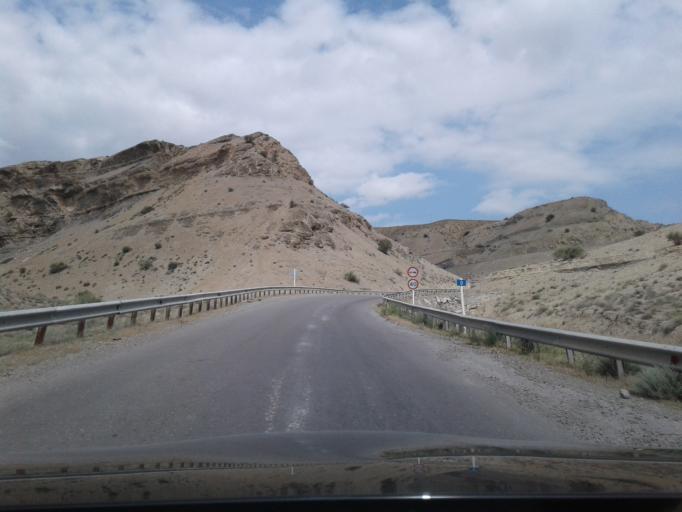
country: TM
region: Ahal
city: Baharly
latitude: 38.5048
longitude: 57.0798
